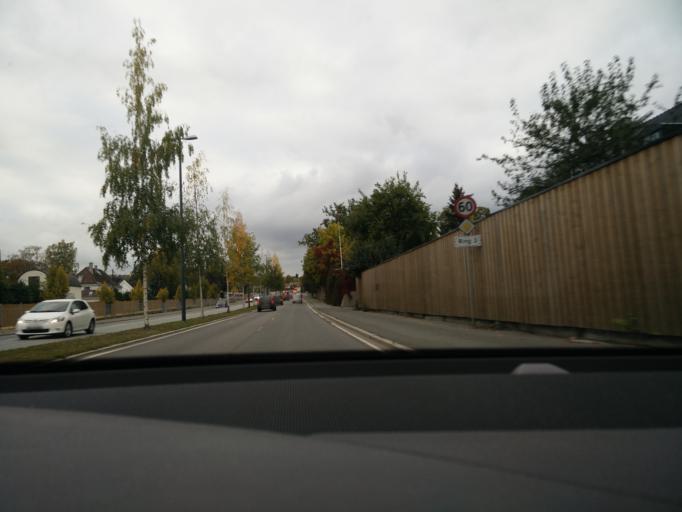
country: NO
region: Oslo
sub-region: Oslo
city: Sjolyststranda
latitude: 59.9361
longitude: 10.6900
